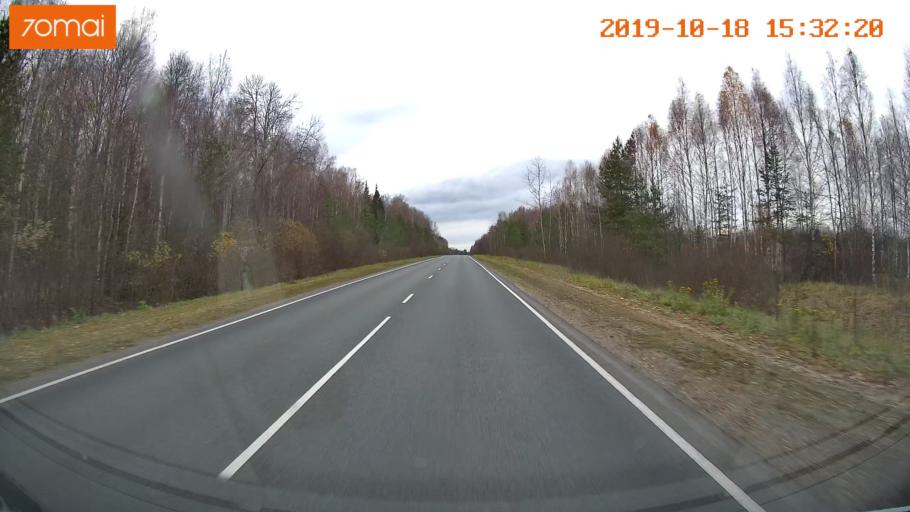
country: RU
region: Vladimir
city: Anopino
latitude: 55.8247
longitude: 40.6555
